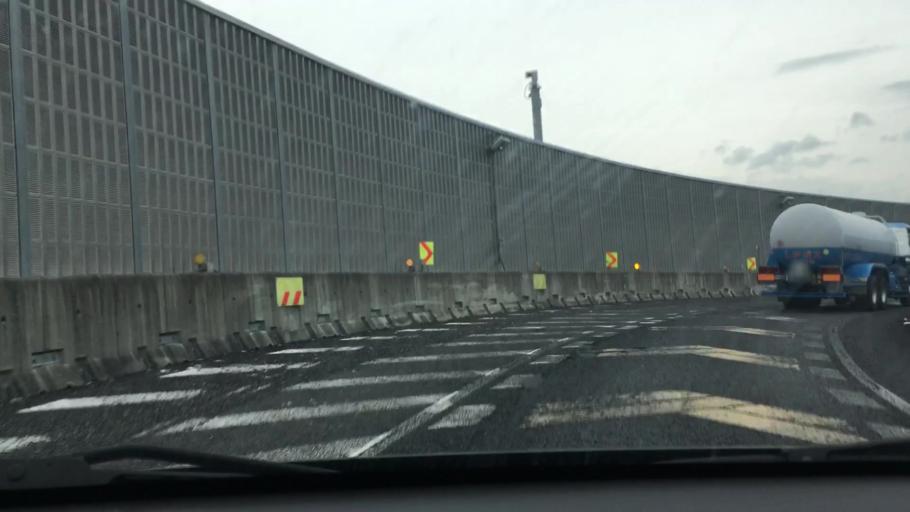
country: JP
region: Mie
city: Kameyama
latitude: 34.8569
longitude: 136.4147
